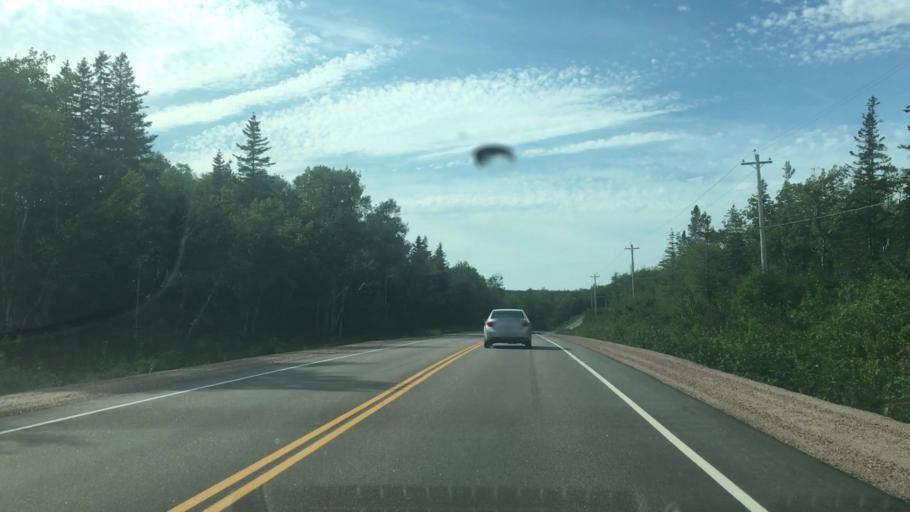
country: CA
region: Nova Scotia
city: Sydney Mines
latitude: 46.8199
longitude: -60.3524
